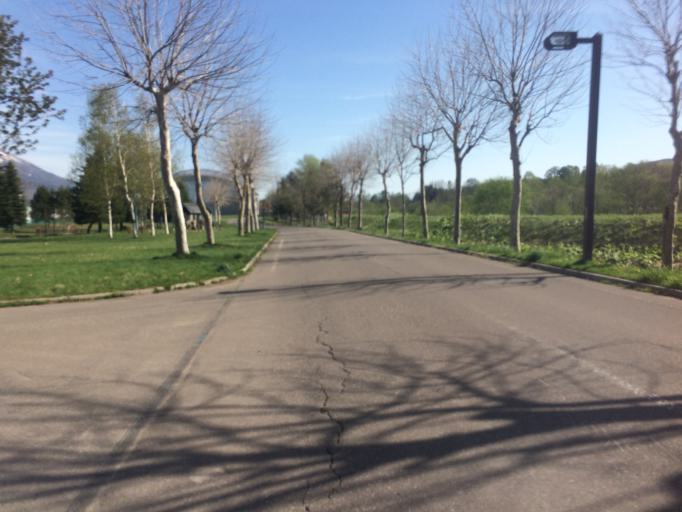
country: JP
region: Hokkaido
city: Niseko Town
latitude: 42.9038
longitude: 140.7441
